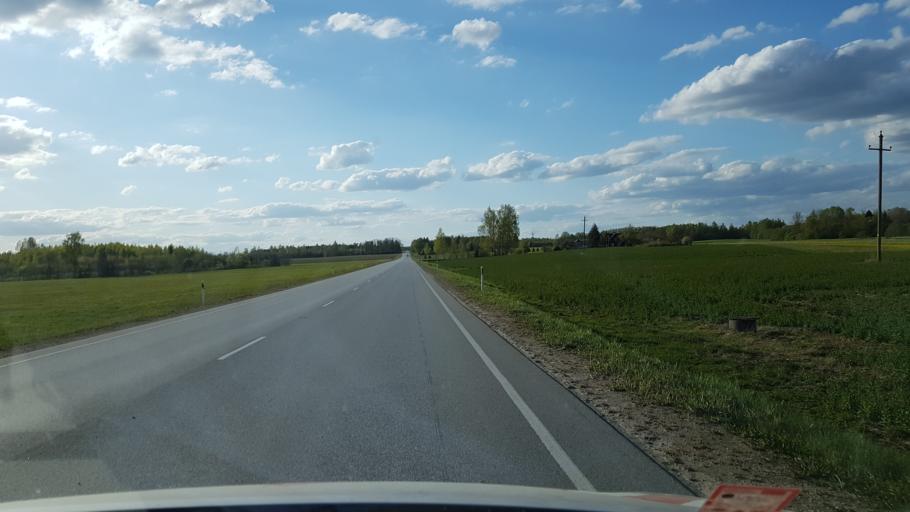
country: EE
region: Vorumaa
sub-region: Voru linn
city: Voru
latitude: 57.9079
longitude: 26.8287
